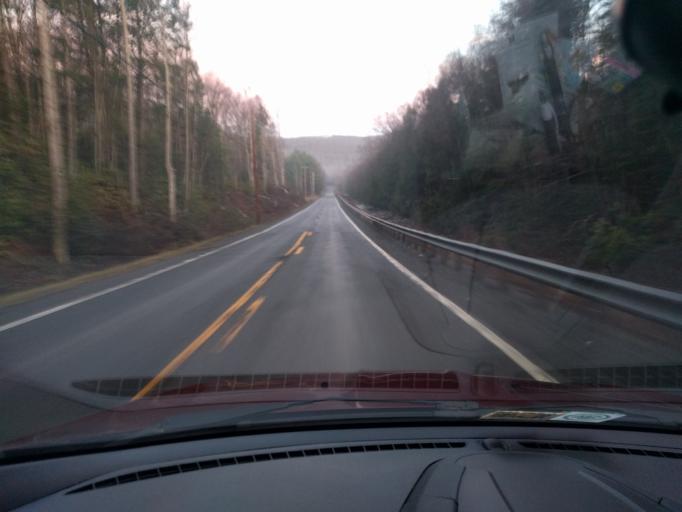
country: US
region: West Virginia
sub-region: Greenbrier County
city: Rainelle
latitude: 38.0444
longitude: -80.9242
